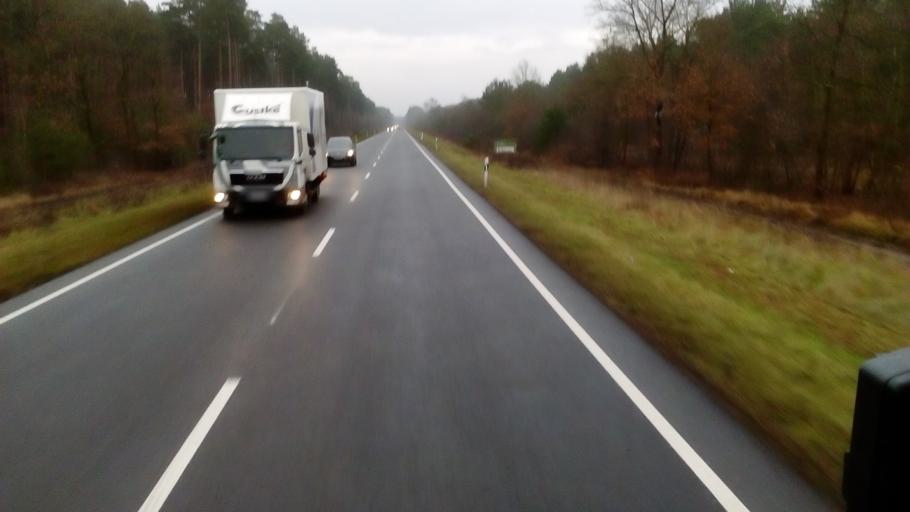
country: DE
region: Brandenburg
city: Weisen
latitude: 53.0389
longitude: 11.8087
